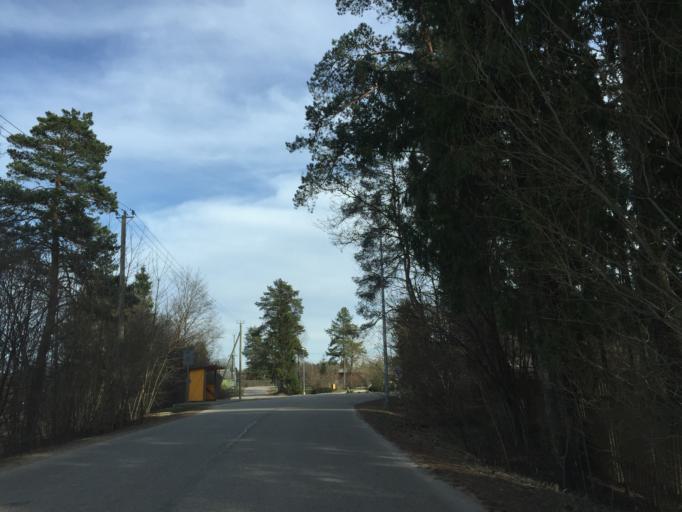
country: LV
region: Ogre
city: Ogre
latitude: 56.8102
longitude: 24.6326
